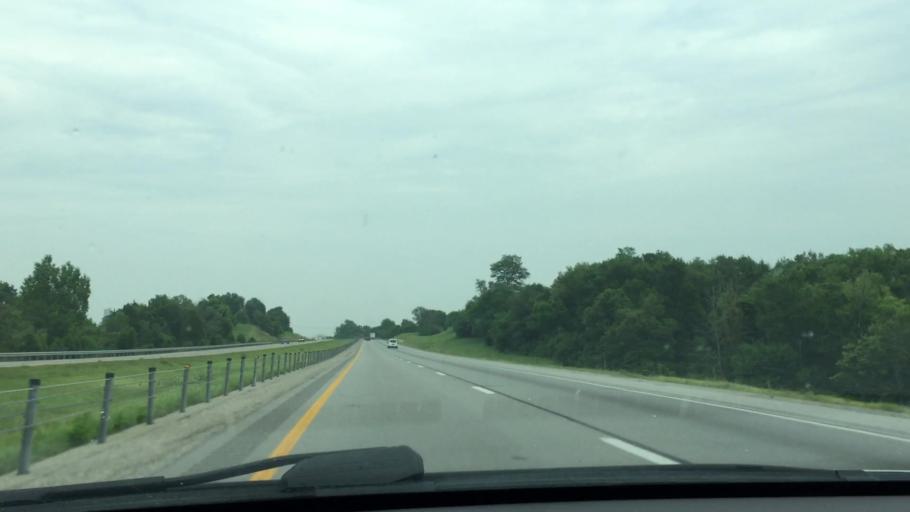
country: US
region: Indiana
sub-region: Switzerland County
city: Vevay
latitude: 38.6631
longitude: -85.0326
